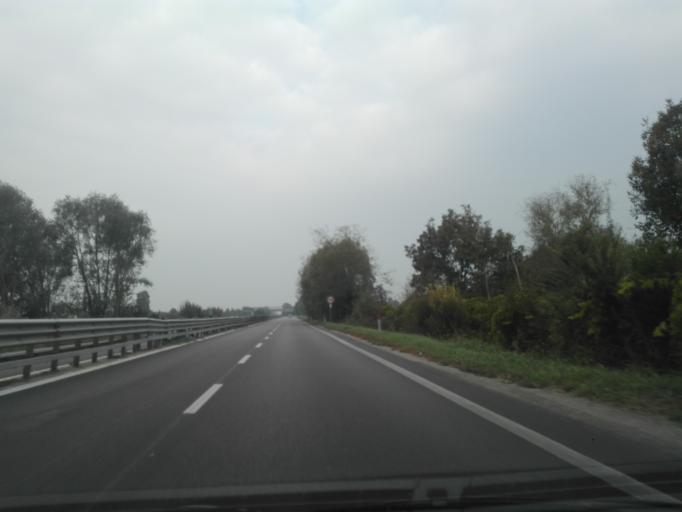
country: IT
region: Veneto
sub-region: Provincia di Verona
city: Villa Bartolomea
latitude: 45.1454
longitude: 11.3487
